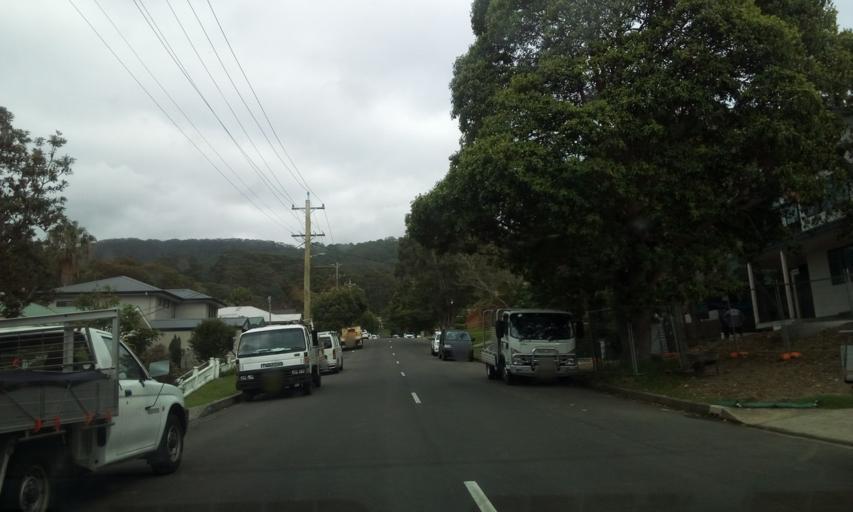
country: AU
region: New South Wales
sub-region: Wollongong
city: Bulli
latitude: -34.3168
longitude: 150.9129
